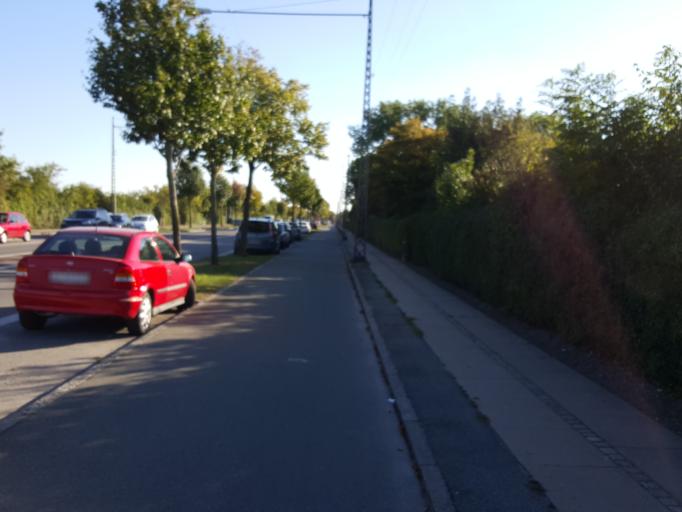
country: DK
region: Capital Region
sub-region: Tarnby Kommune
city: Tarnby
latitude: 55.6248
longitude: 12.5867
